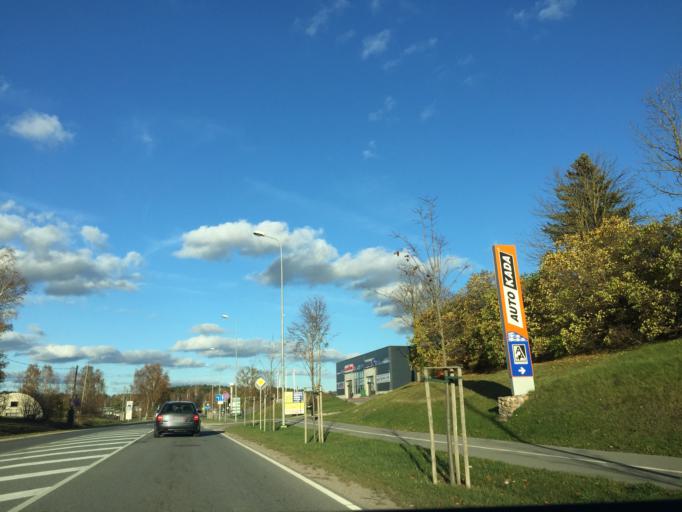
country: LV
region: Tukuma Rajons
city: Tukums
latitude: 56.9535
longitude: 23.1180
